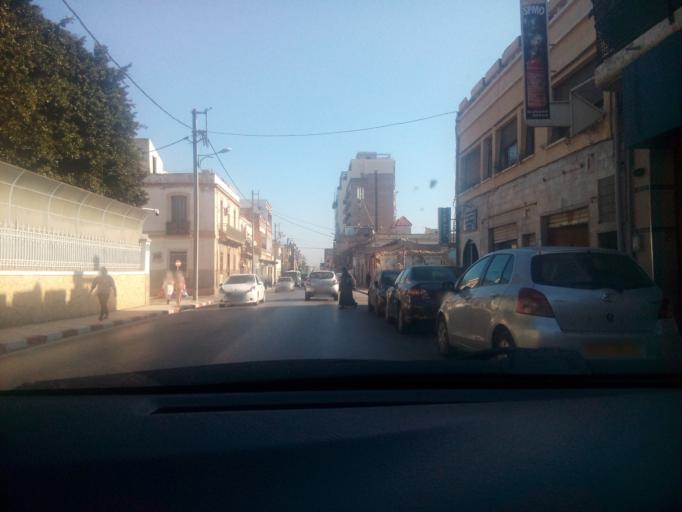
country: DZ
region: Oran
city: Oran
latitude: 35.6882
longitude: -0.6636
